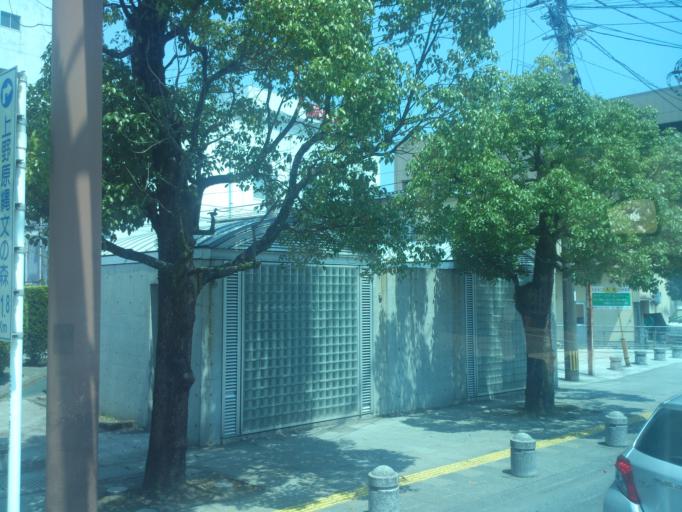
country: JP
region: Kagoshima
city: Kokubu-matsuki
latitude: 31.7391
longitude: 130.7656
